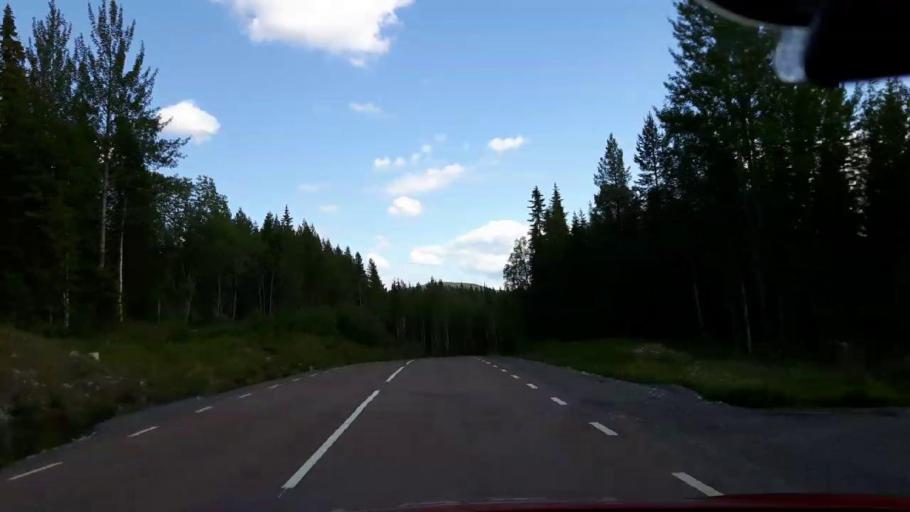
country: SE
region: Jaemtland
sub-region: Krokoms Kommun
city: Valla
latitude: 64.0541
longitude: 14.1676
